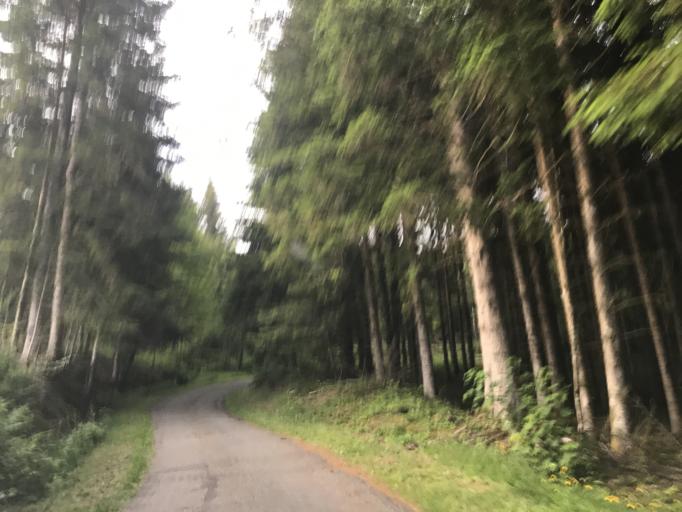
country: FR
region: Rhone-Alpes
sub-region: Departement de la Loire
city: Noiretable
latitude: 45.7699
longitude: 3.7172
